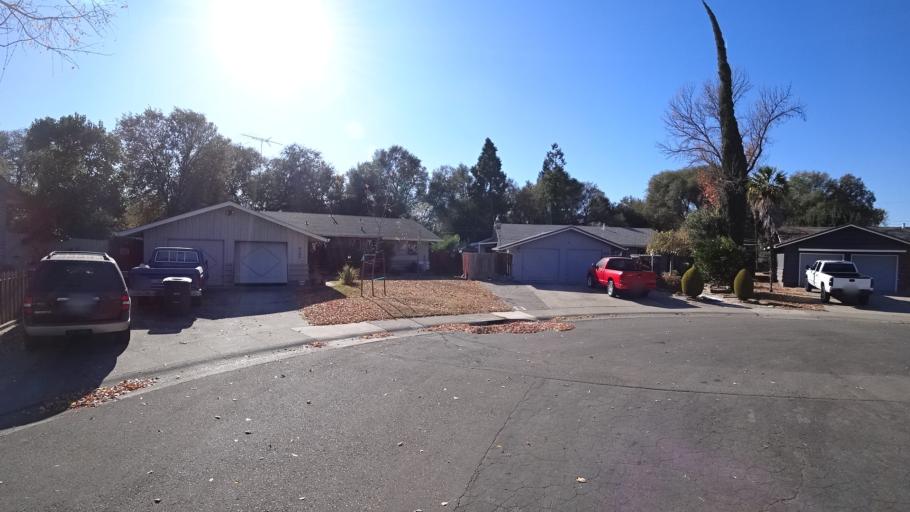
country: US
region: California
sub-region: Sacramento County
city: Antelope
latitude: 38.6756
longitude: -121.3121
